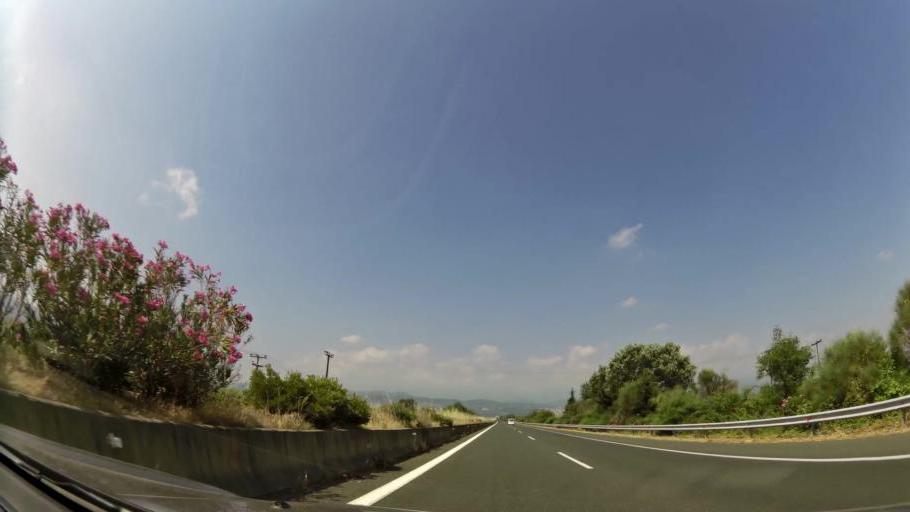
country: GR
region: Central Macedonia
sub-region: Nomos Imathias
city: Diavatos
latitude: 40.5300
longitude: 22.2869
